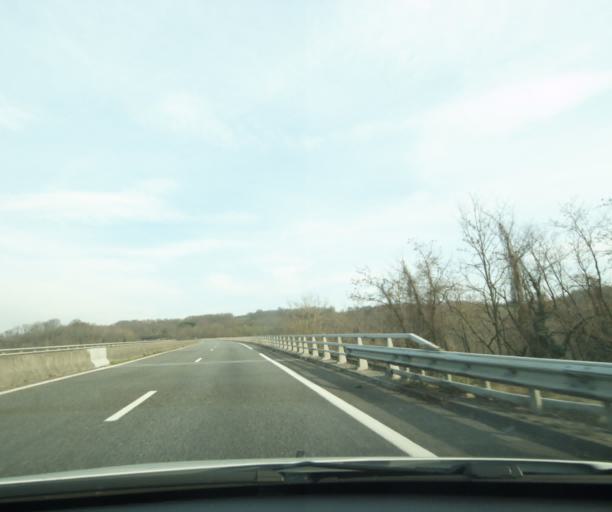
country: FR
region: Midi-Pyrenees
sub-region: Departement des Hautes-Pyrenees
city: Tournay
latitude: 43.1975
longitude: 0.1875
